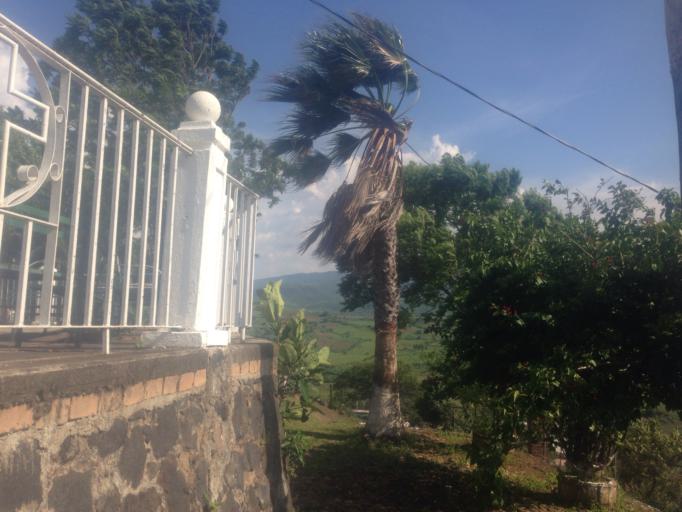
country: MX
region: Nayarit
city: Ixtlan del Rio
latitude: 21.0357
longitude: -104.3578
